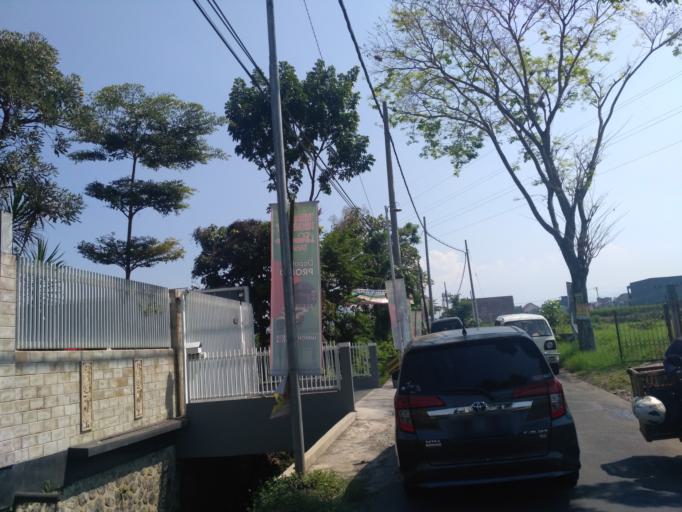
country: ID
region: East Java
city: Batu
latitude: -7.9091
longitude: 112.5867
